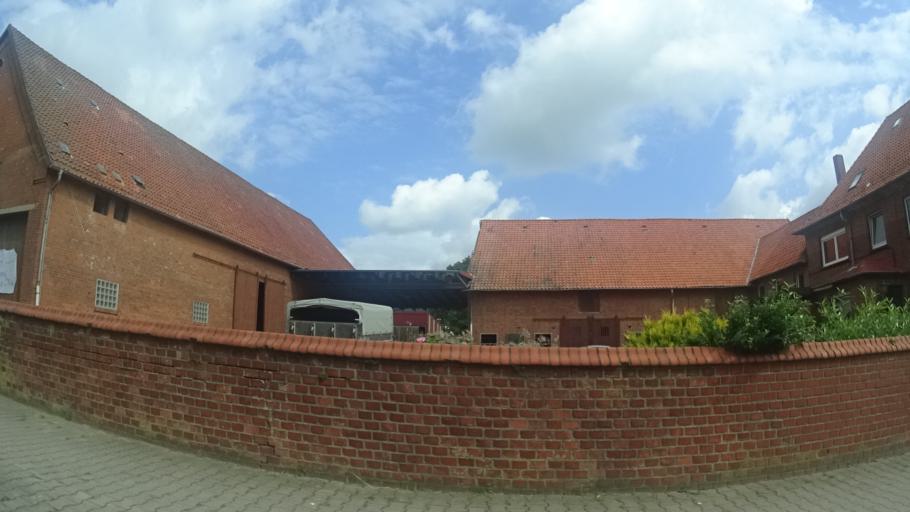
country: DE
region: Lower Saxony
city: Ronnenberg
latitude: 52.2394
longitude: 9.6613
